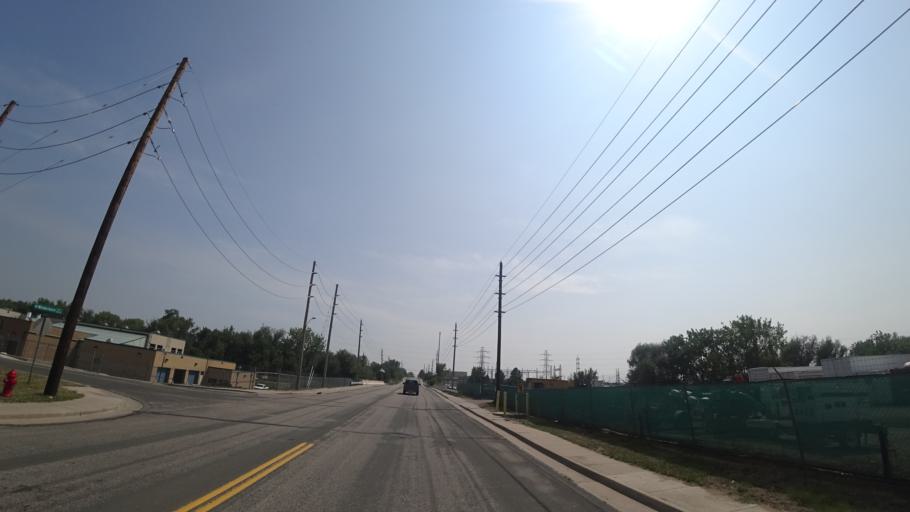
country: US
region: Colorado
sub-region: Arapahoe County
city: Littleton
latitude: 39.6298
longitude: -105.0067
